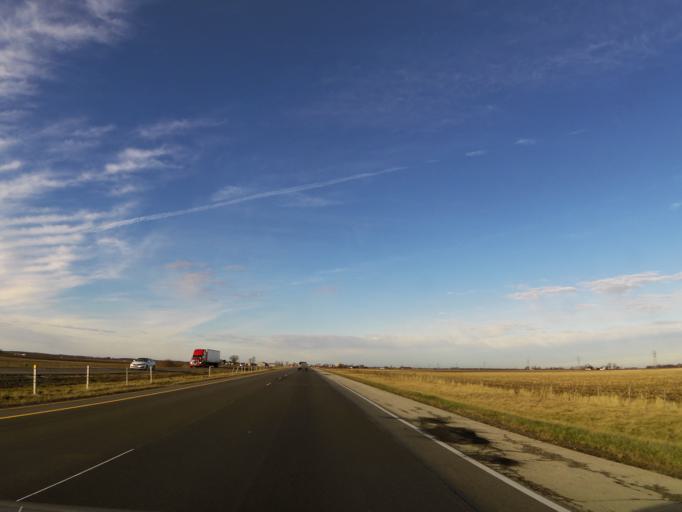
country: US
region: Illinois
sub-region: Vermilion County
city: Oakwood
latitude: 40.1265
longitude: -87.7881
